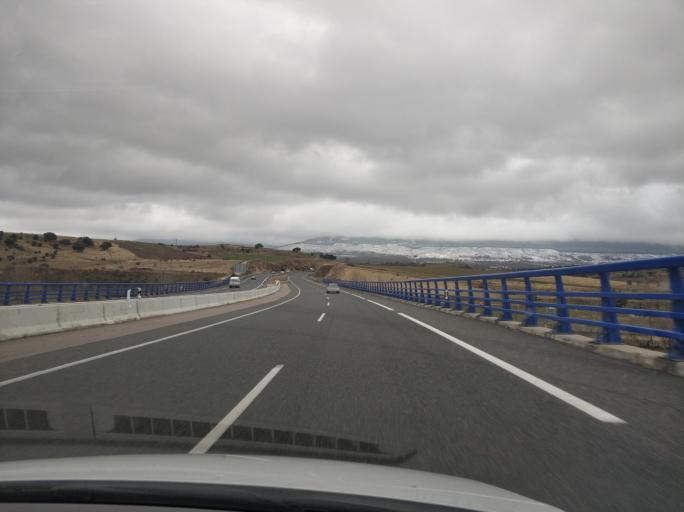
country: ES
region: Castille and Leon
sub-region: Provincia de Segovia
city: Cerezo de Abajo
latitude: 41.2228
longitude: -3.5887
